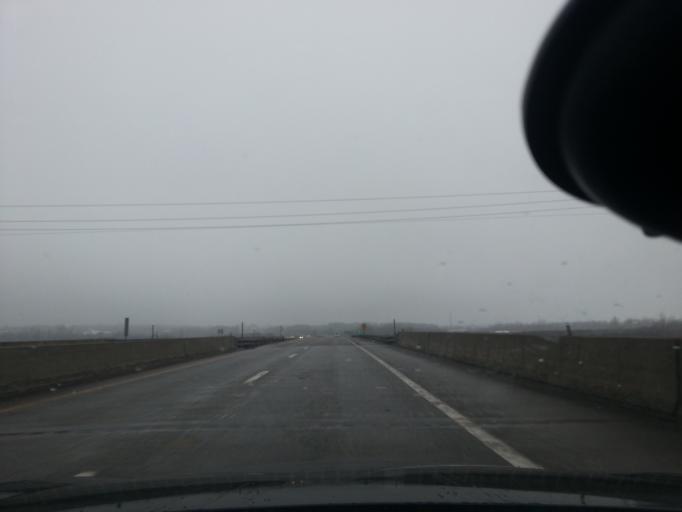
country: US
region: New York
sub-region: Jefferson County
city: Watertown
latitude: 44.0013
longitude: -75.9193
